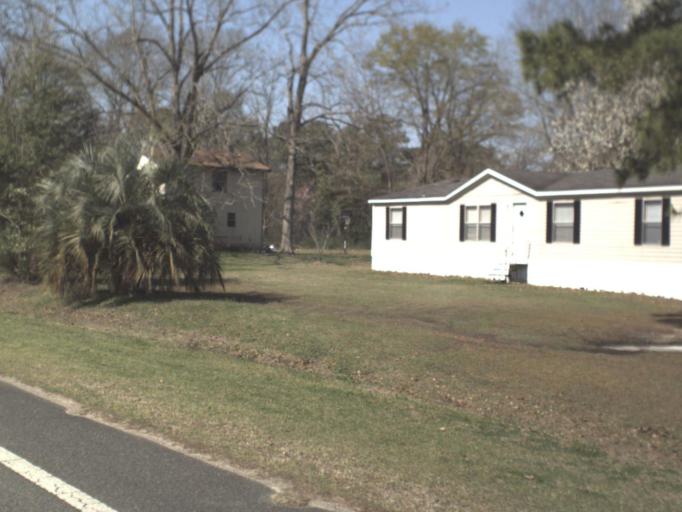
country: US
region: Florida
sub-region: Gadsden County
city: Havana
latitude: 30.6147
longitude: -84.4515
